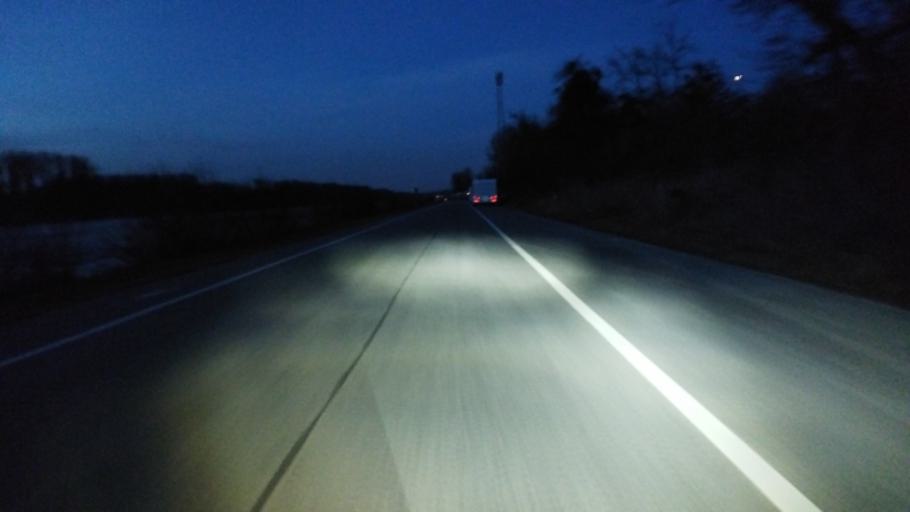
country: DE
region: Rheinland-Pfalz
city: Leimersheim
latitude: 49.1184
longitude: 8.3663
